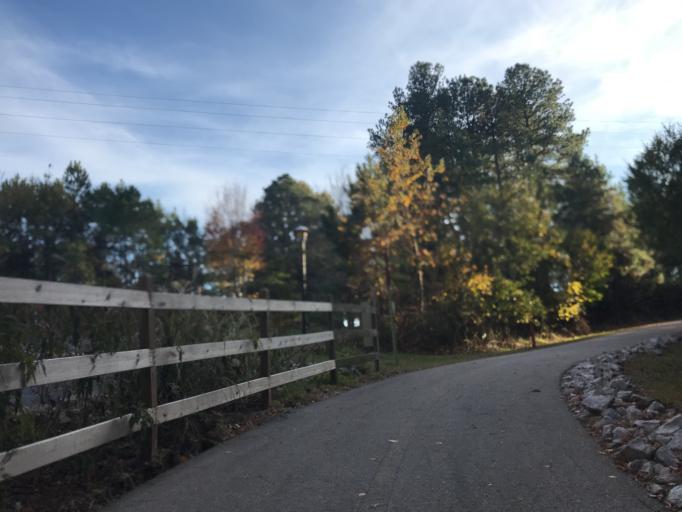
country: US
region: North Carolina
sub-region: Wake County
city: West Raleigh
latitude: 35.8025
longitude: -78.6916
